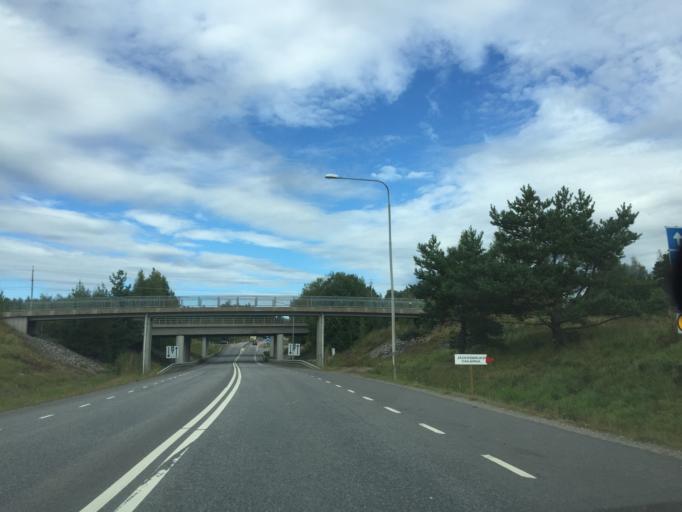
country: SE
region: Vaestmanland
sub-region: Arboga Kommun
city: Arboga
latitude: 59.4031
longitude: 15.8884
